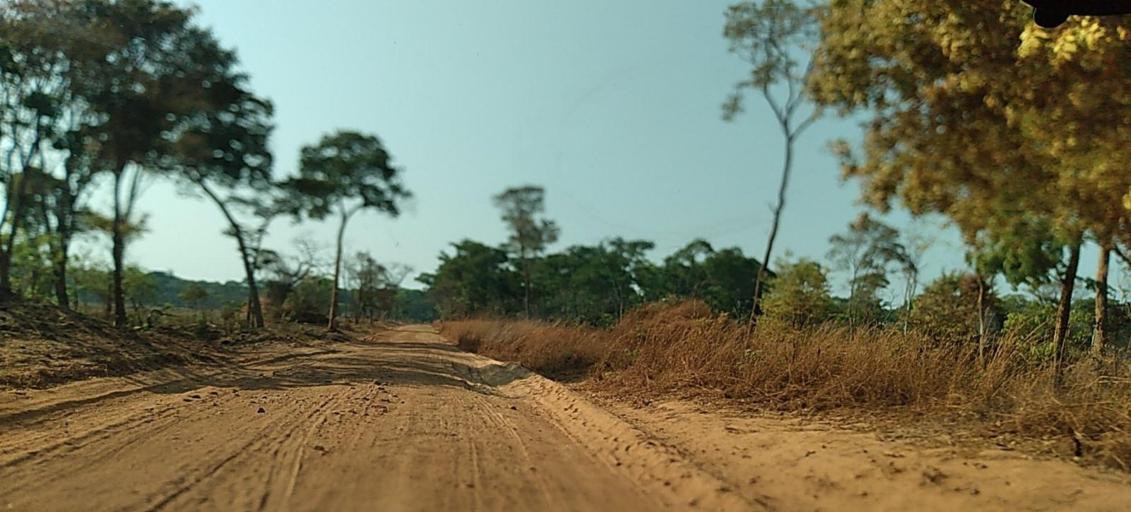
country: ZM
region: North-Western
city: Kasempa
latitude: -13.6487
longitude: 26.0026
